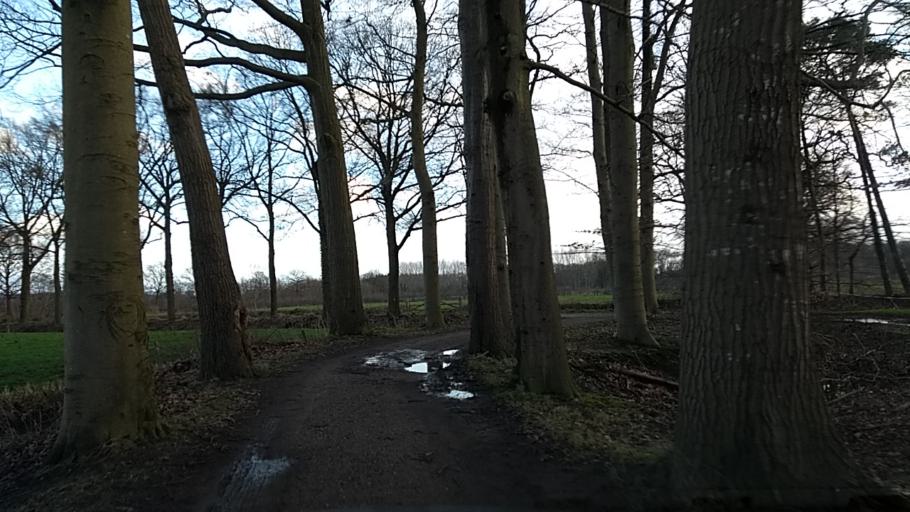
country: NL
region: Overijssel
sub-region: Gemeente Deventer
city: Schalkhaar
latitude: 52.2597
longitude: 6.2464
